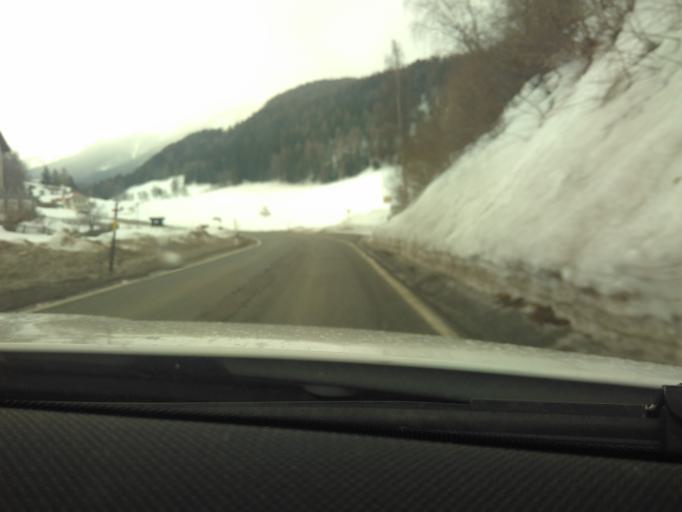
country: CH
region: Grisons
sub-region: Inn District
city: Scuol
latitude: 46.7821
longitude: 10.2692
